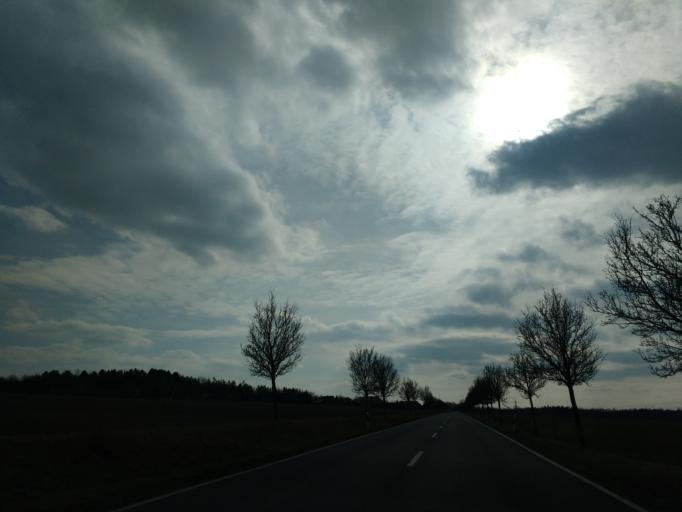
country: DE
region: Saxony-Anhalt
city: Schraplau
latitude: 51.4455
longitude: 11.6643
